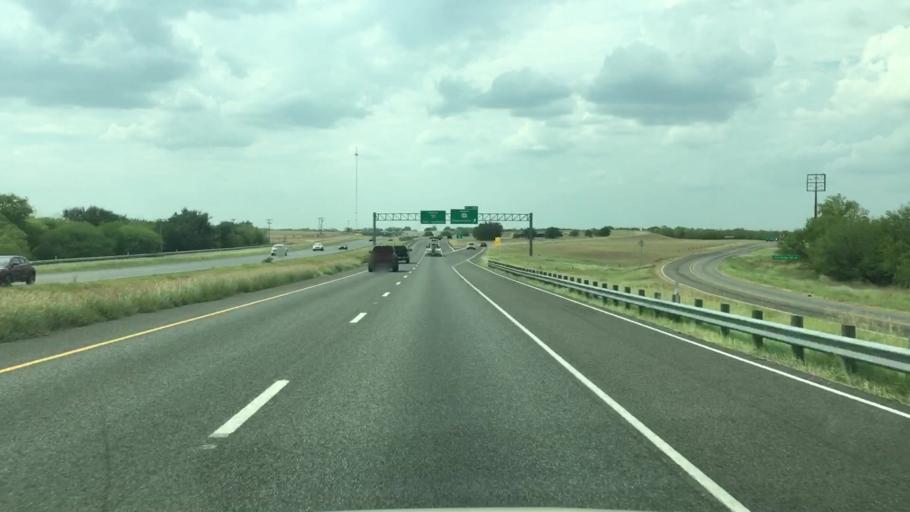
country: US
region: Texas
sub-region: Atascosa County
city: Pleasanton
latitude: 28.9050
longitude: -98.4280
